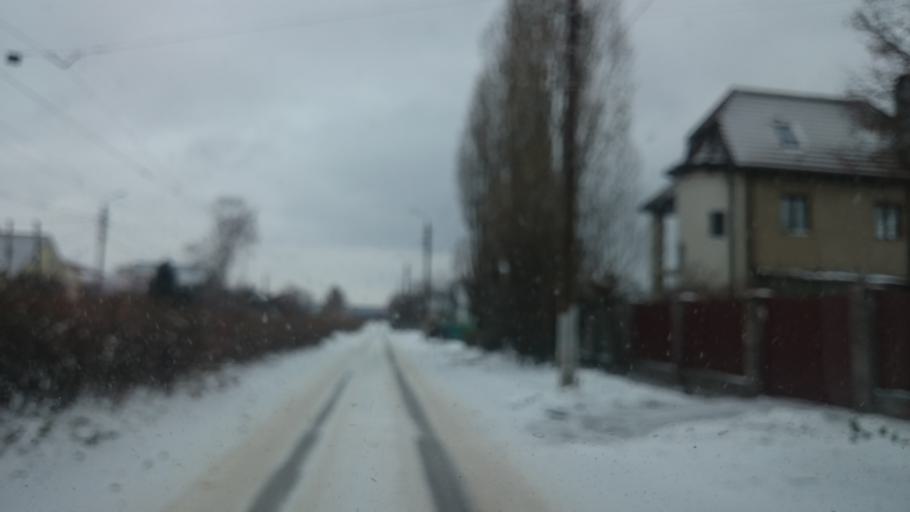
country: RU
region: Tula
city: Tula
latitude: 54.2008
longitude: 37.5588
